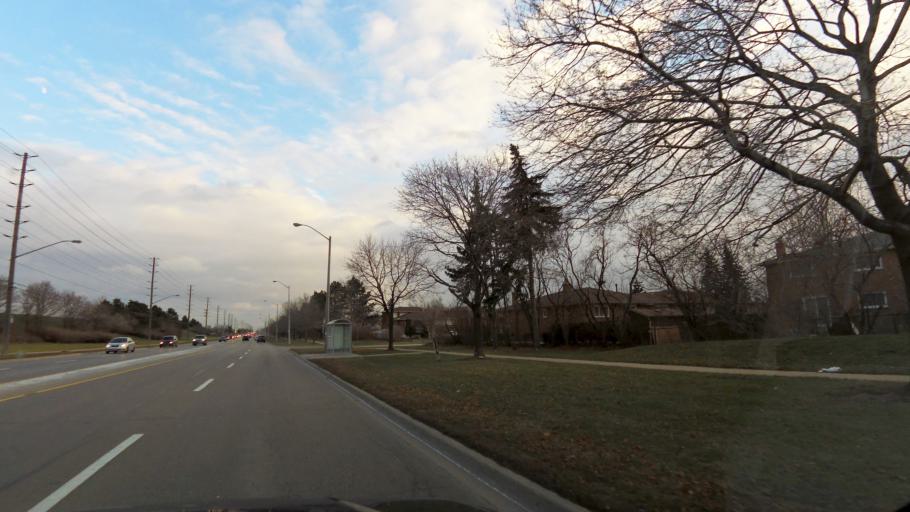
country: CA
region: Ontario
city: Brampton
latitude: 43.7472
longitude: -79.7244
